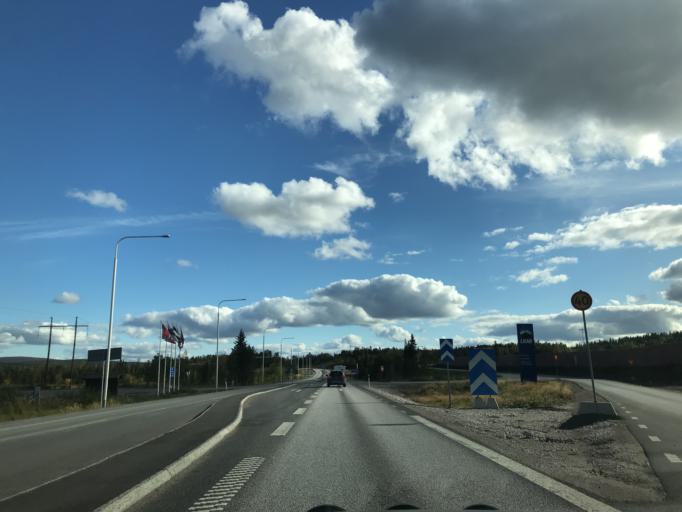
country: SE
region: Norrbotten
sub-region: Gallivare Kommun
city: Malmberget
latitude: 67.6530
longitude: 21.0156
